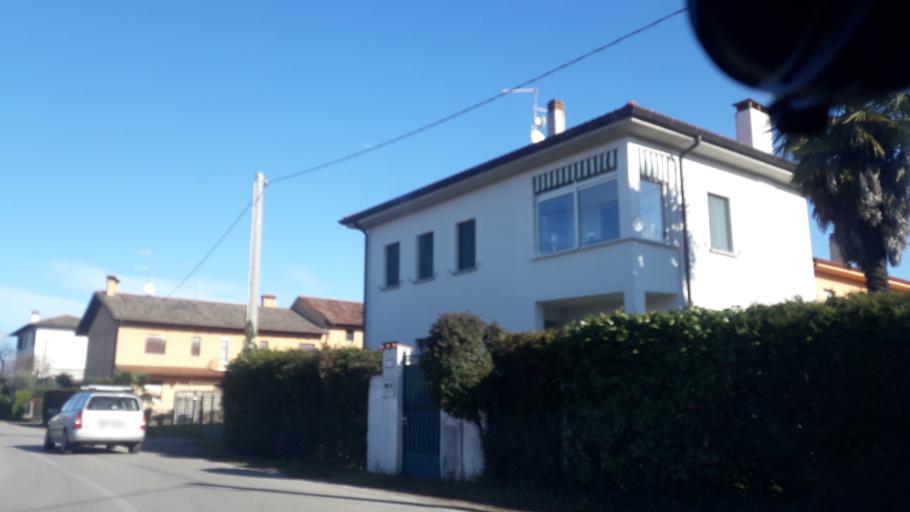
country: IT
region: Friuli Venezia Giulia
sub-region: Provincia di Udine
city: Udine
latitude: 46.0428
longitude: 13.2364
